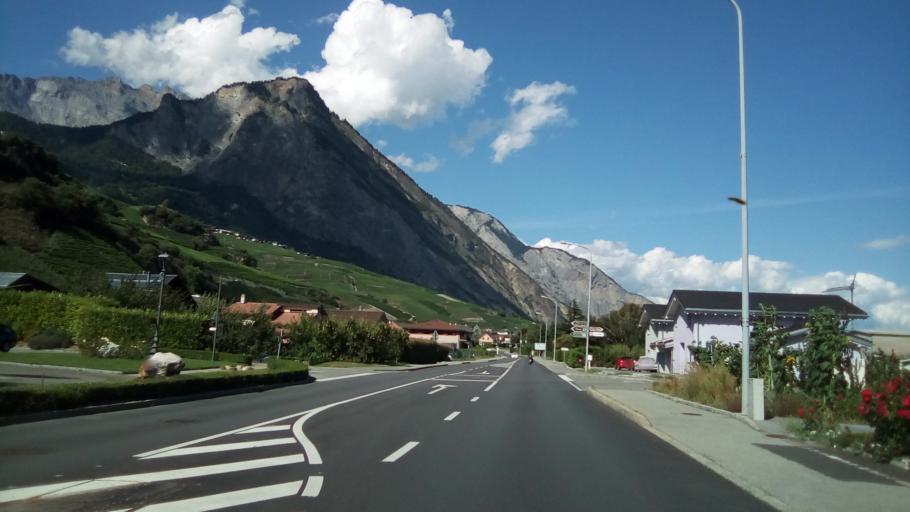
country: CH
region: Valais
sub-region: Martigny District
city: Saillon
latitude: 46.1735
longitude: 7.1891
